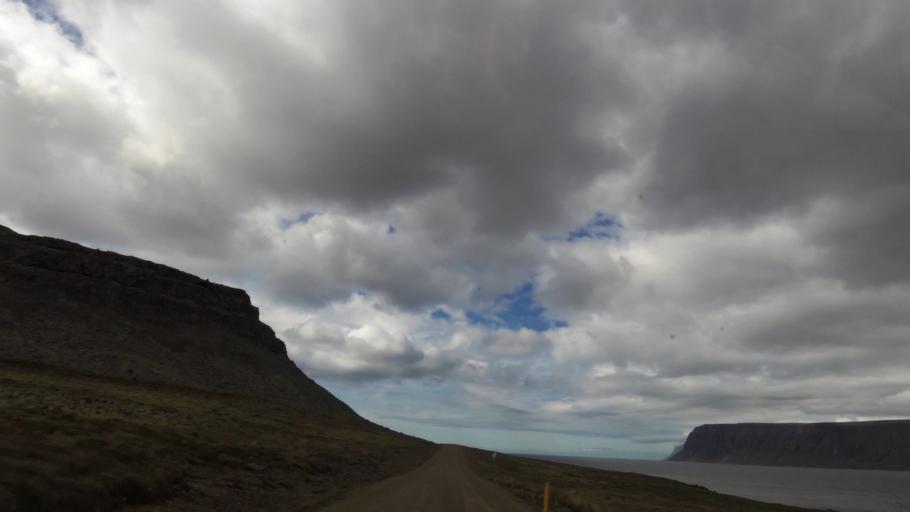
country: IS
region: West
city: Olafsvik
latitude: 65.5725
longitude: -24.0628
